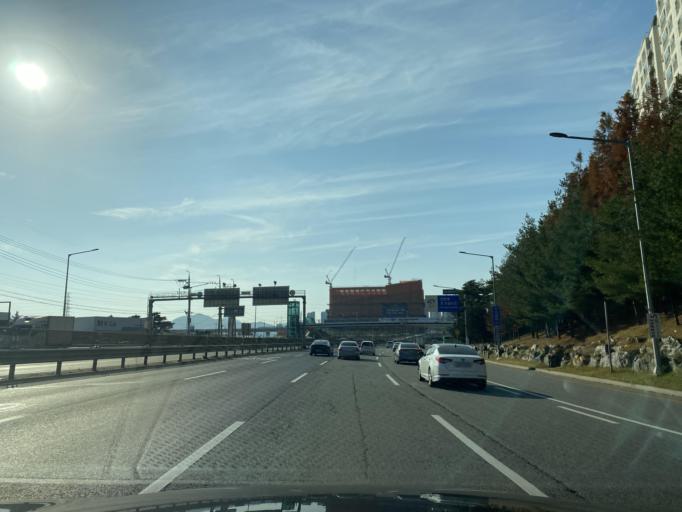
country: KR
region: Chungcheongnam-do
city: Cheonan
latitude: 36.7850
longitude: 127.1149
